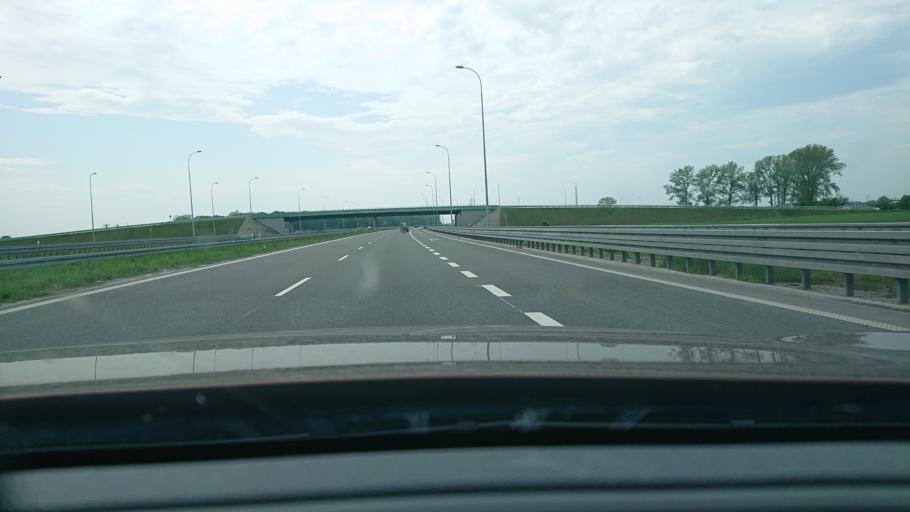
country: PL
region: Subcarpathian Voivodeship
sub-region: Powiat lancucki
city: Czarna
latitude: 50.0909
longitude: 22.1607
